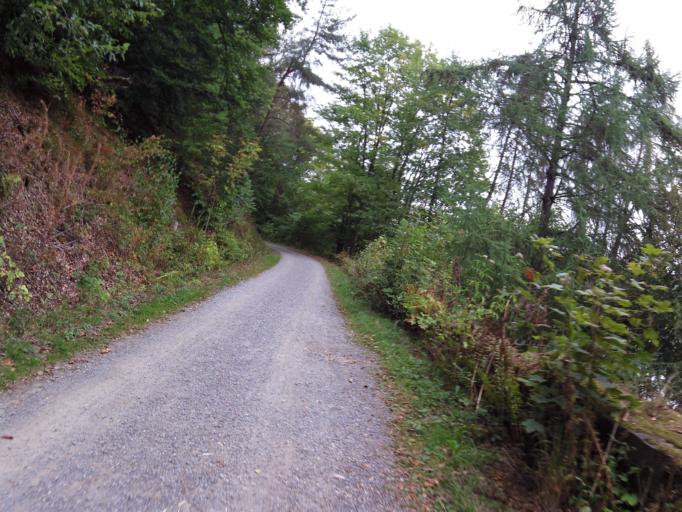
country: DE
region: North Rhine-Westphalia
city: Heimbach
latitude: 50.6332
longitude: 6.4398
